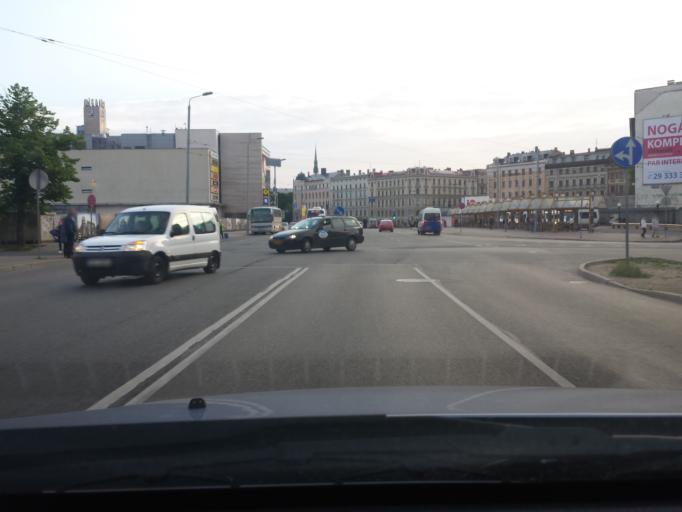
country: LV
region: Riga
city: Riga
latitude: 56.9480
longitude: 24.1234
